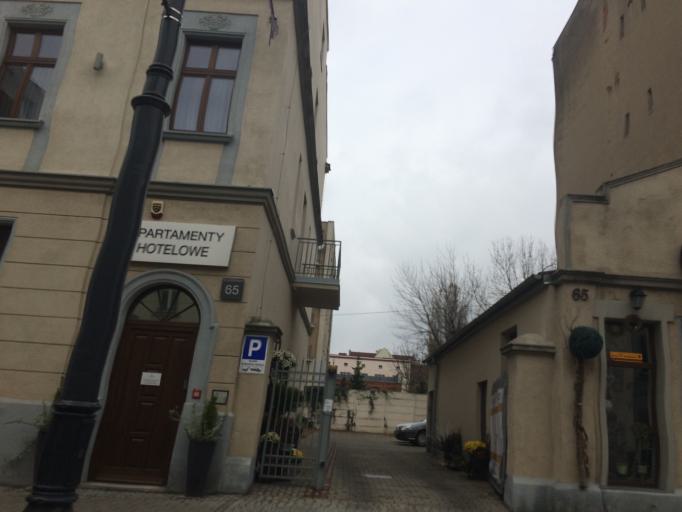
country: PL
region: Lodz Voivodeship
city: Lodz
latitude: 51.7579
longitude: 19.4370
